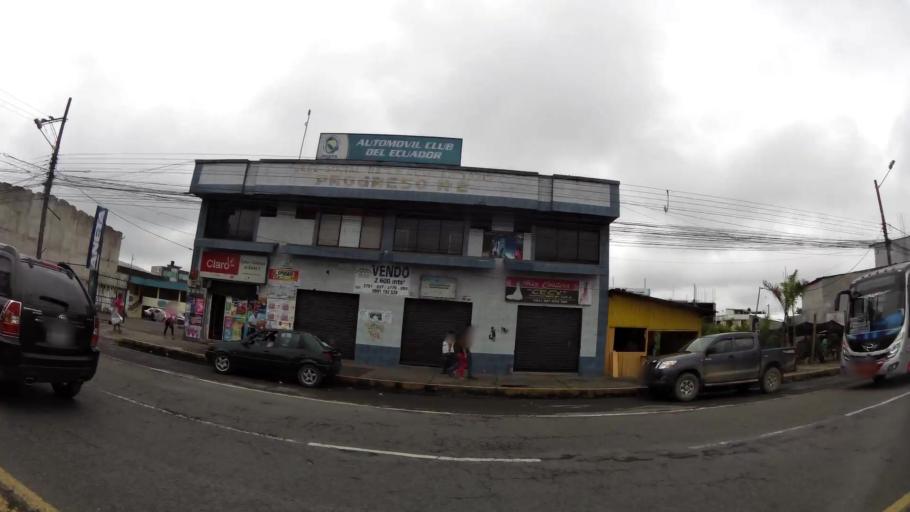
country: EC
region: Santo Domingo de los Tsachilas
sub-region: Canton Santo Domingo de los Colorados
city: Santo Domingo de los Colorados
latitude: -0.2436
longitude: -79.1683
